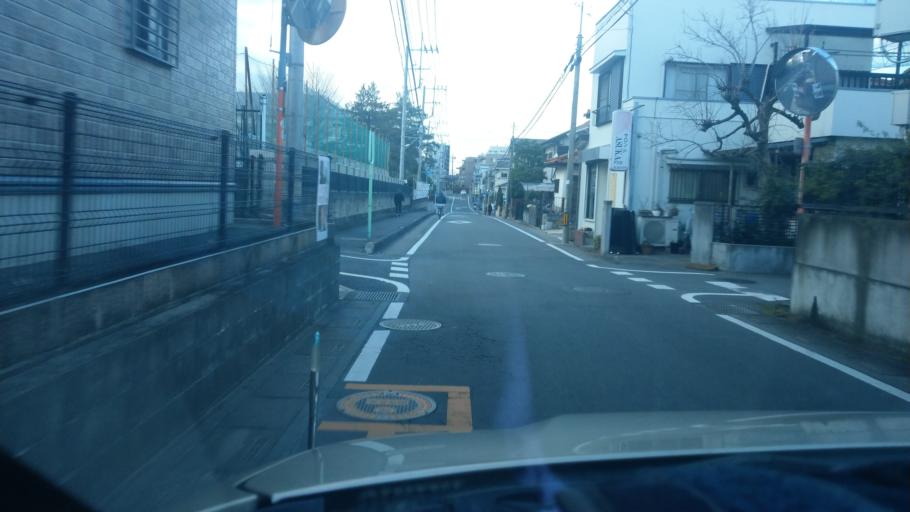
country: JP
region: Saitama
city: Yono
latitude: 35.8951
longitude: 139.6005
